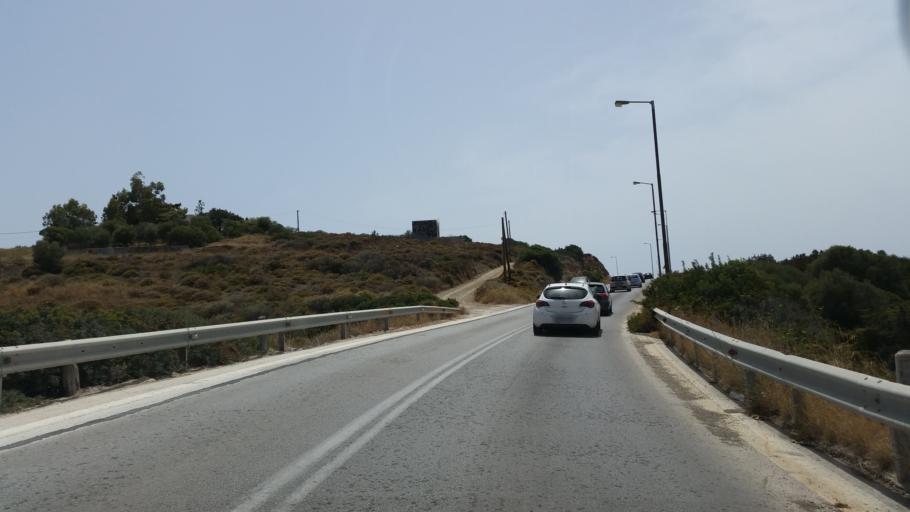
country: GR
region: Attica
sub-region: Nomarchia Anatolikis Attikis
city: Palaia Fokaia
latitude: 37.7005
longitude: 23.9399
